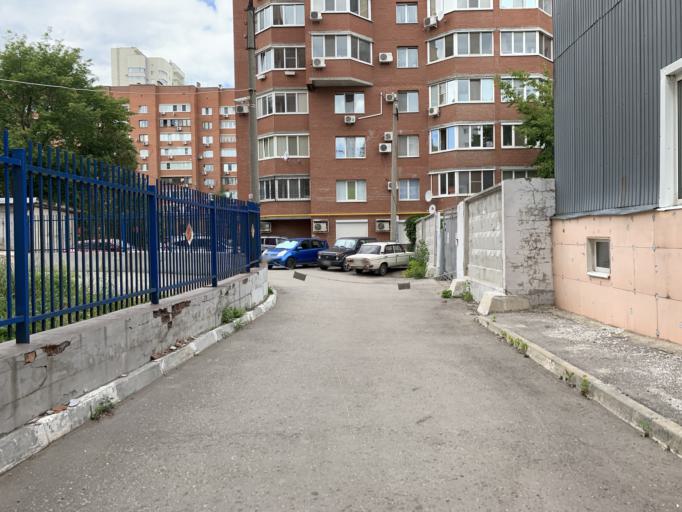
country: RU
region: Samara
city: Samara
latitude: 53.2155
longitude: 50.1697
